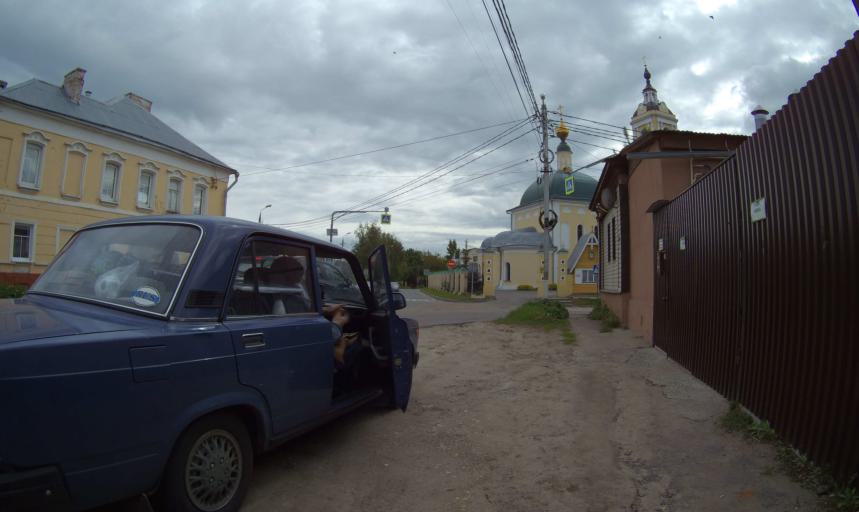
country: RU
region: Moskovskaya
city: Kolomna
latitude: 55.0982
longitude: 38.7511
